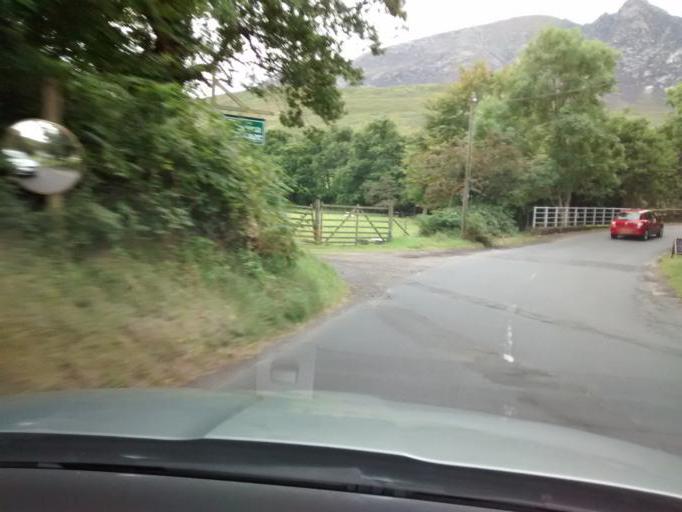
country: GB
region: Scotland
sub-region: North Ayrshire
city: Isle of Arran
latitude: 55.6635
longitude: -5.1559
